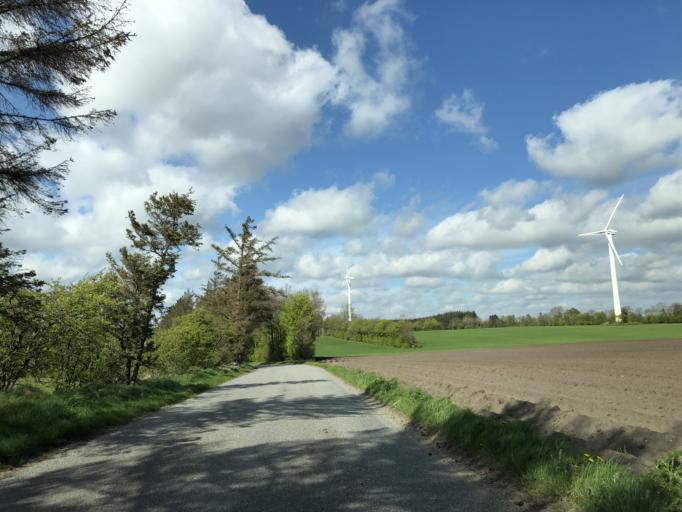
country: DK
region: Central Jutland
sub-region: Herning Kommune
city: Avlum
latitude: 56.2803
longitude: 8.6971
